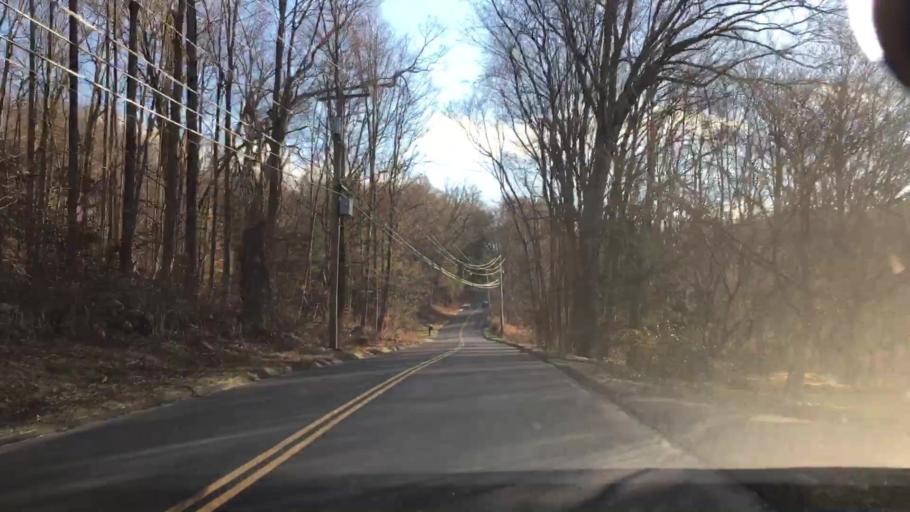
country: US
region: Connecticut
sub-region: Fairfield County
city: Newtown
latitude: 41.4378
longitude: -73.3146
